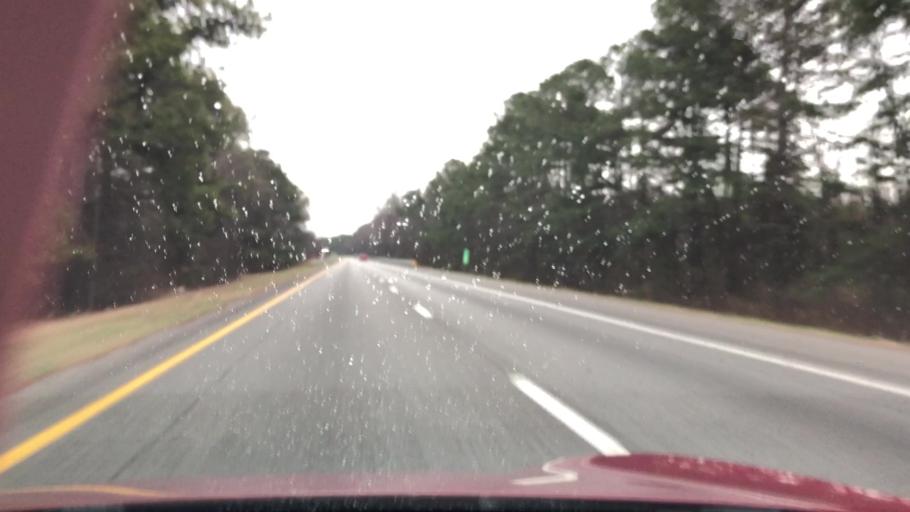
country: US
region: South Carolina
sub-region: Dillon County
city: Latta
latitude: 34.3553
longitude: -79.5136
